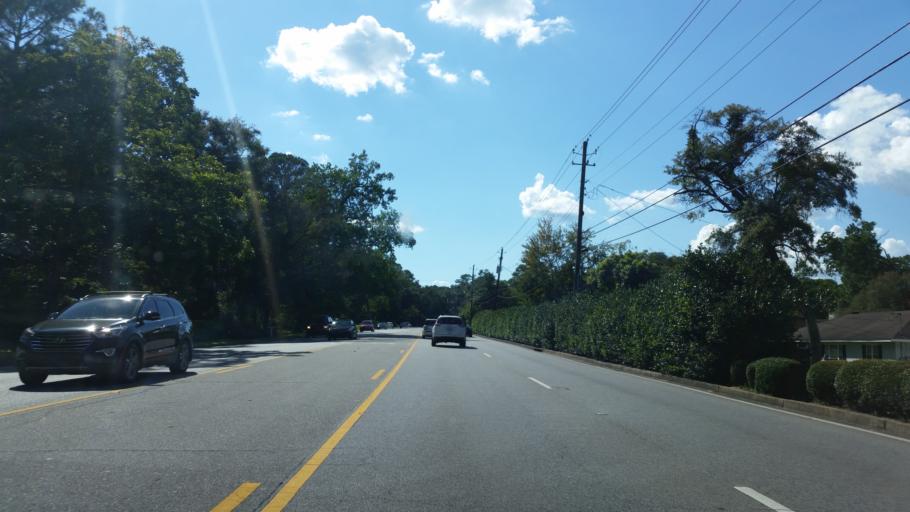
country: US
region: Alabama
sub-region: Mobile County
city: Prichard
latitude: 30.7043
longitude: -88.1293
